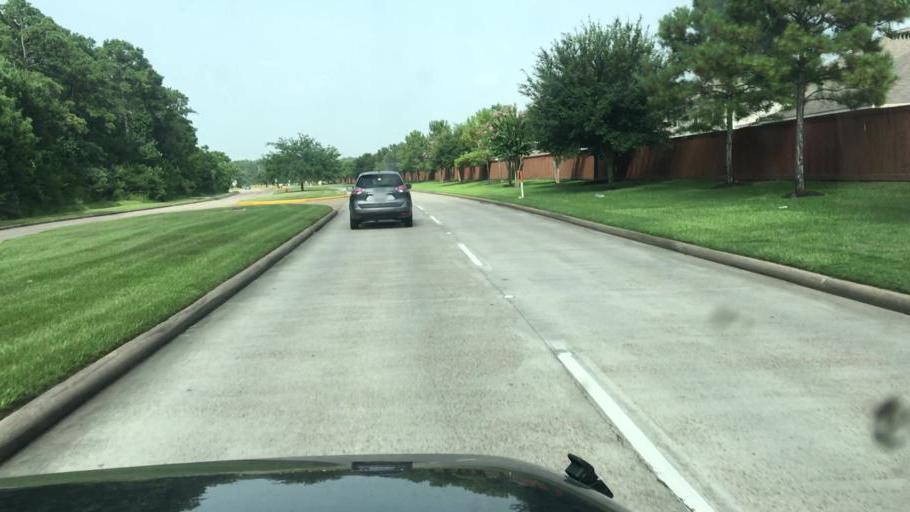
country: US
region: Texas
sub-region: Harris County
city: Atascocita
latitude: 29.9779
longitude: -95.2023
